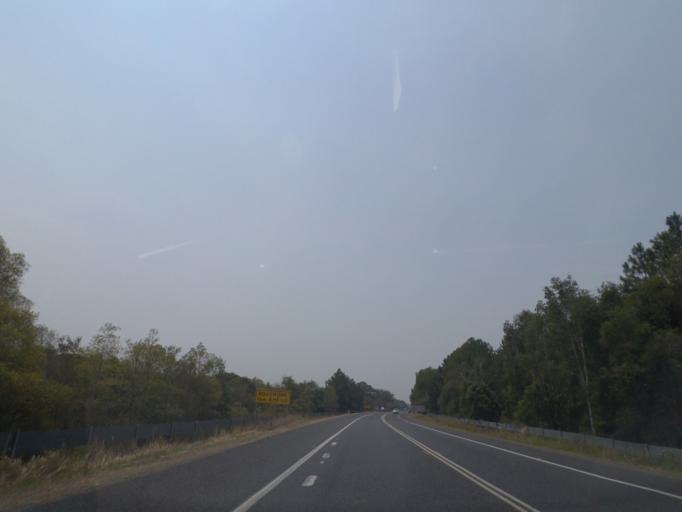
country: AU
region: New South Wales
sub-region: Ballina
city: Ballina
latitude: -28.9372
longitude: 153.4708
